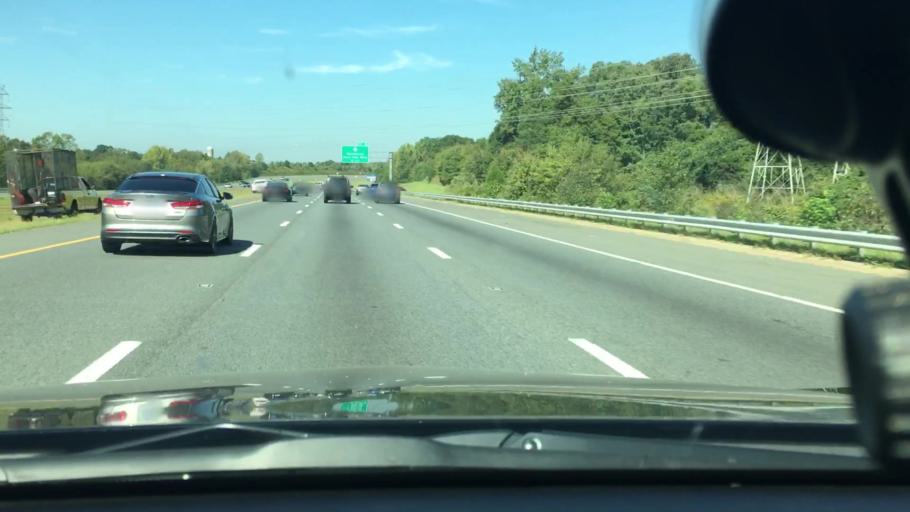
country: US
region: North Carolina
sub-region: Cabarrus County
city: Harrisburg
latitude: 35.3078
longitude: -80.6978
